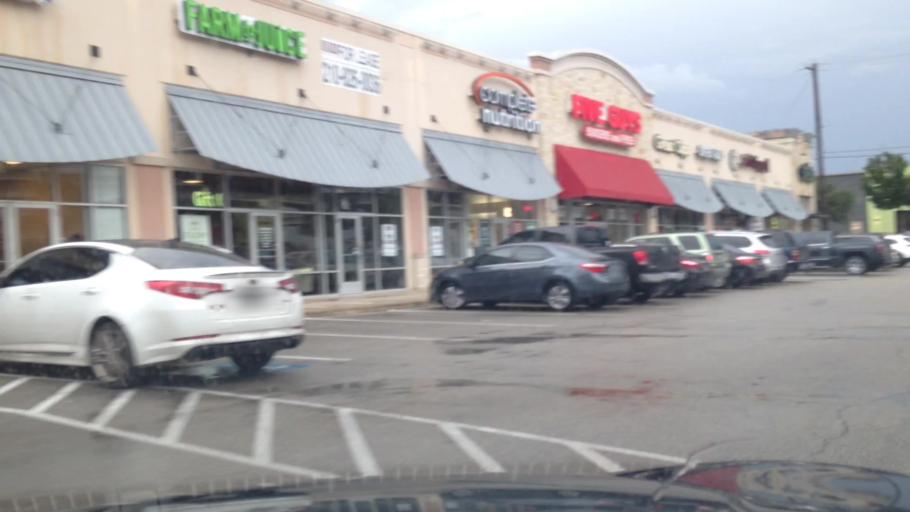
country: US
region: Texas
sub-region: Bexar County
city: Hollywood Park
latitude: 29.6109
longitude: -98.4742
